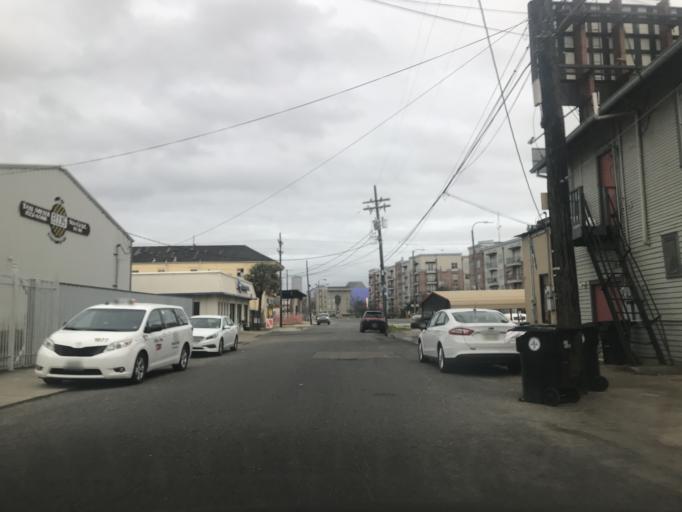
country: US
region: Louisiana
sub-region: Orleans Parish
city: New Orleans
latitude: 29.9648
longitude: -90.0965
